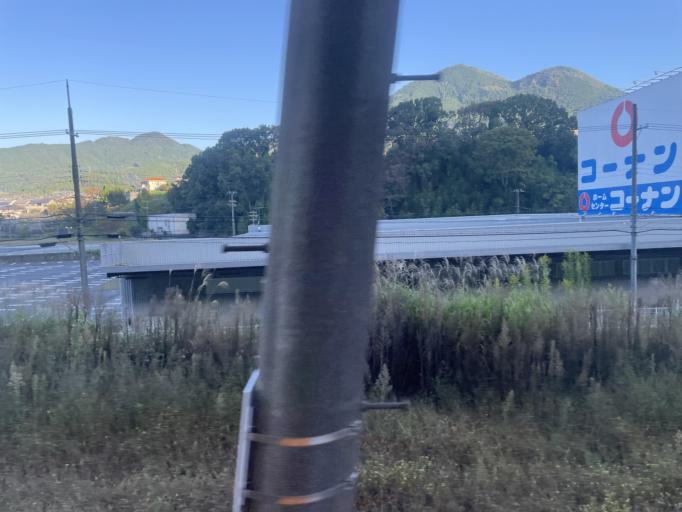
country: JP
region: Nara
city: Haibara-akanedai
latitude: 34.5427
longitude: 135.9757
